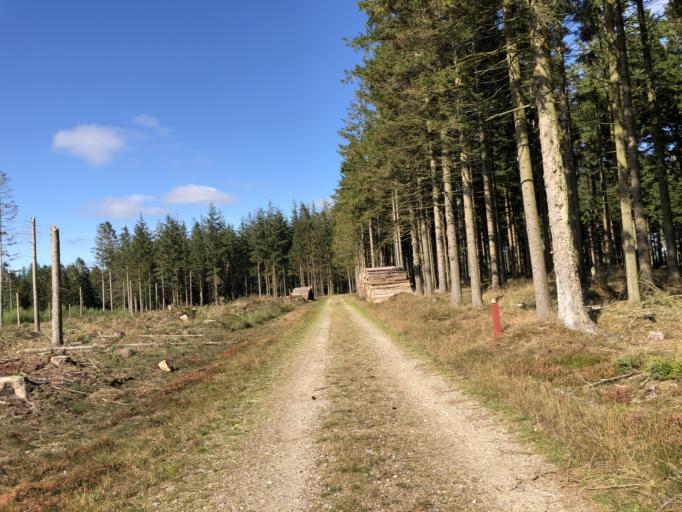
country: DK
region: Central Jutland
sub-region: Holstebro Kommune
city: Holstebro
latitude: 56.2477
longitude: 8.5010
